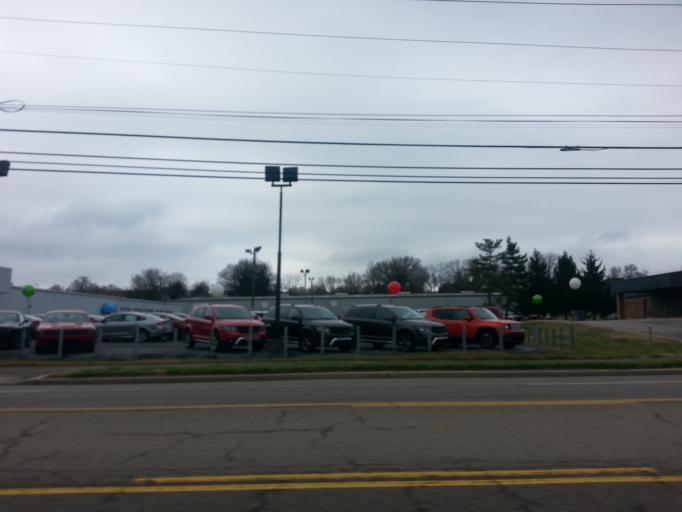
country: US
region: Tennessee
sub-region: Hamblen County
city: Morristown
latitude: 36.2068
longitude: -83.3008
